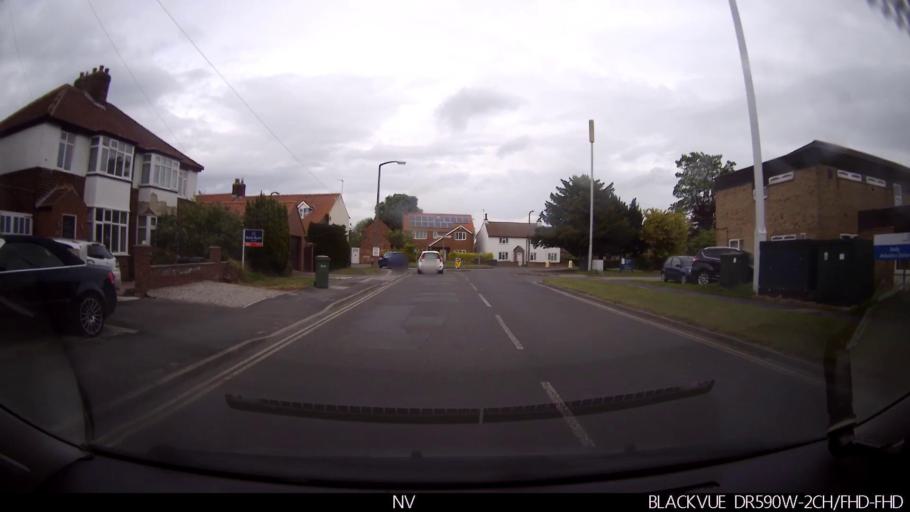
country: GB
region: England
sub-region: City of York
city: Haxby
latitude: 54.0157
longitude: -1.0721
